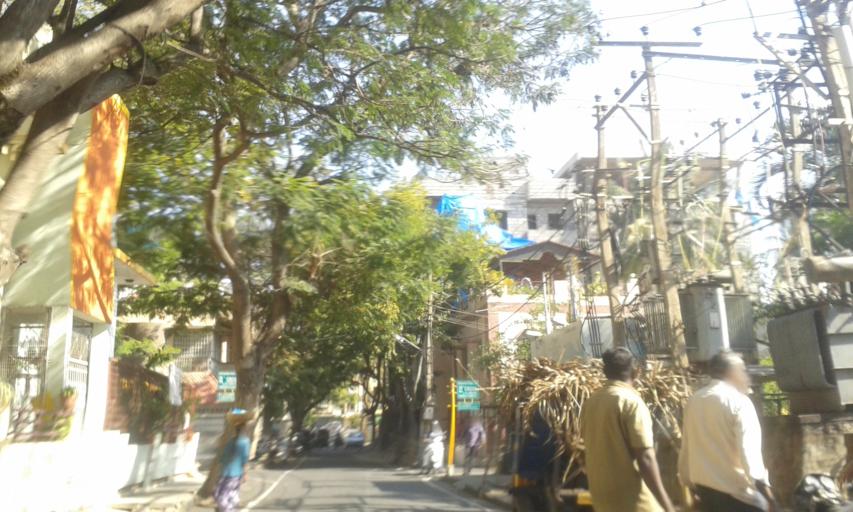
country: IN
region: Karnataka
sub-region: Bangalore Urban
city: Bangalore
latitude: 12.9309
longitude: 77.5899
